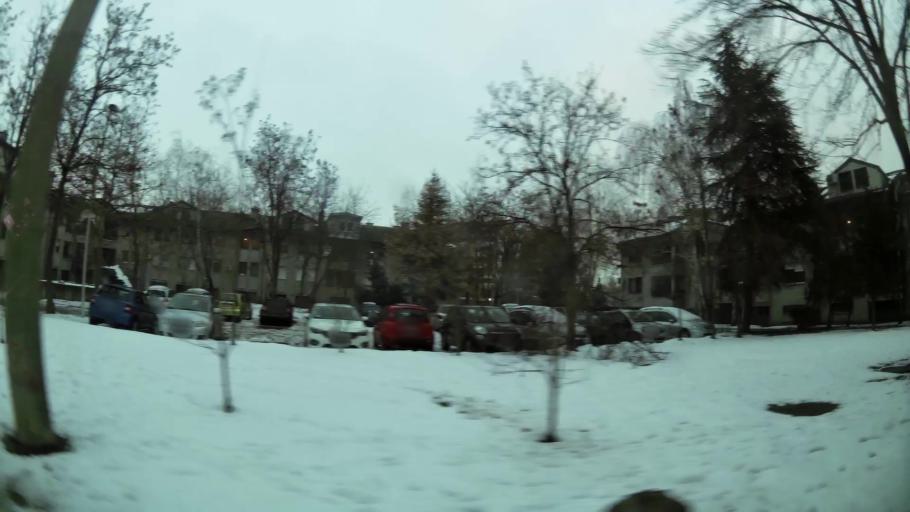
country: RS
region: Central Serbia
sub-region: Belgrade
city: Zemun
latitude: 44.8133
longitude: 20.3770
